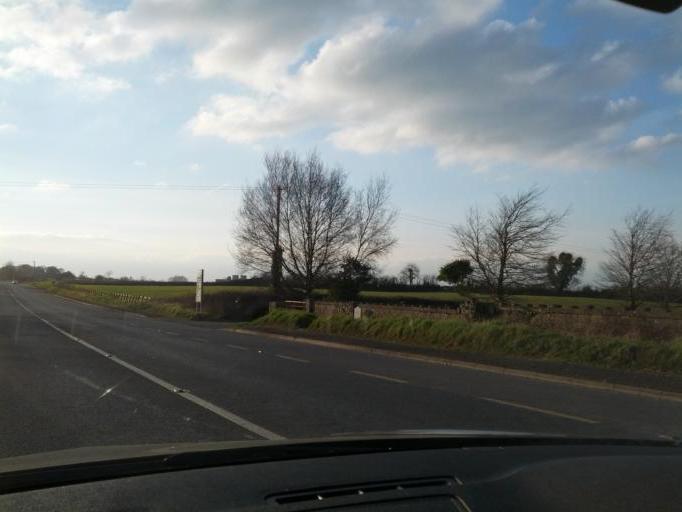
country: IE
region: Munster
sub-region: North Tipperary
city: Nenagh
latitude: 52.8648
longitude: -8.1726
